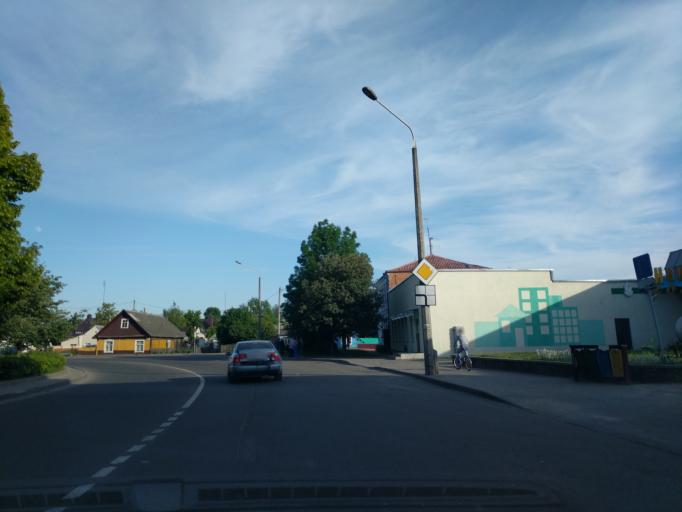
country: BY
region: Grodnenskaya
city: Ashmyany
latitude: 54.4239
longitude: 25.9303
